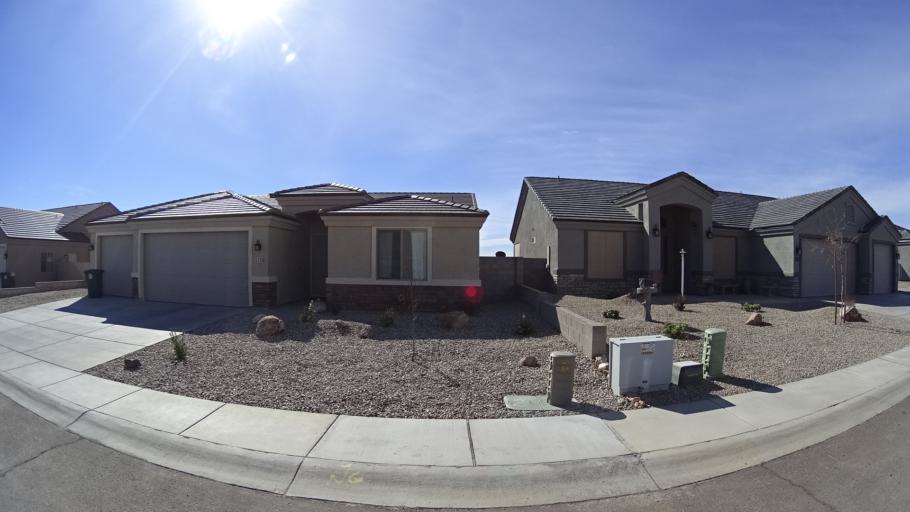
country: US
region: Arizona
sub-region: Mohave County
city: New Kingman-Butler
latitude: 35.2765
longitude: -114.0375
